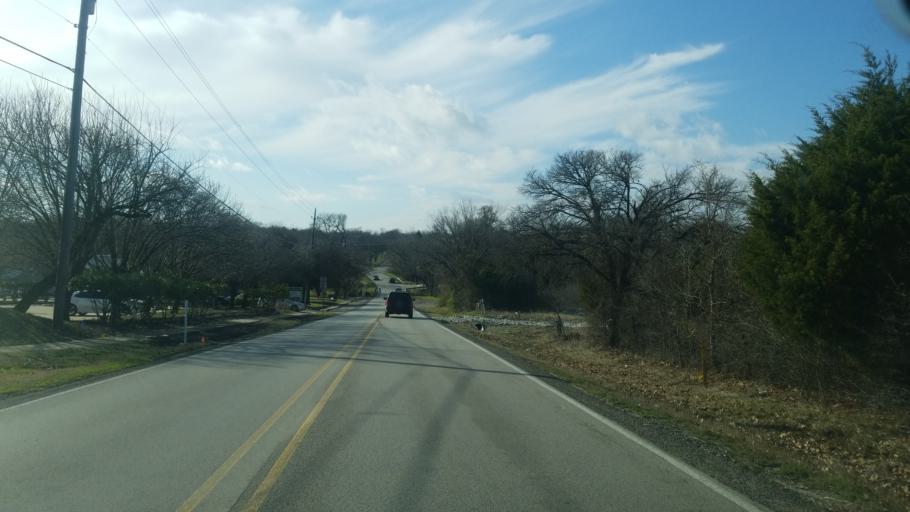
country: US
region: Texas
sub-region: Rockwall County
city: Rockwall
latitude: 32.9364
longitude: -96.4466
